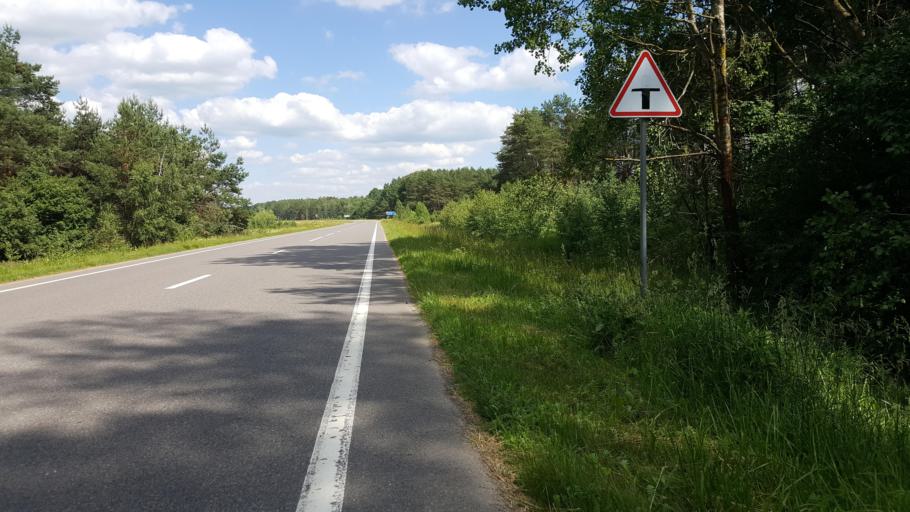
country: BY
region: Brest
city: Kamyanyuki
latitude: 52.5055
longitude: 23.7045
